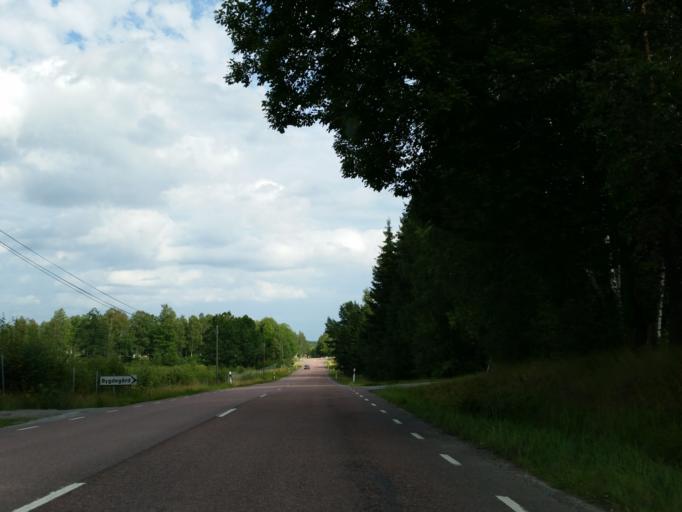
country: SE
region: Soedermanland
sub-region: Strangnas Kommun
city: Mariefred
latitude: 59.2201
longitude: 17.2813
